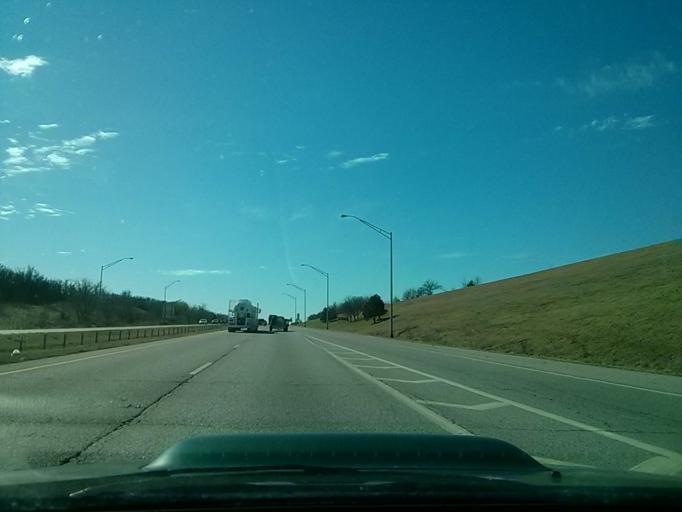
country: US
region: Oklahoma
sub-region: Tulsa County
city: Oakhurst
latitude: 36.0848
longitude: -96.0067
